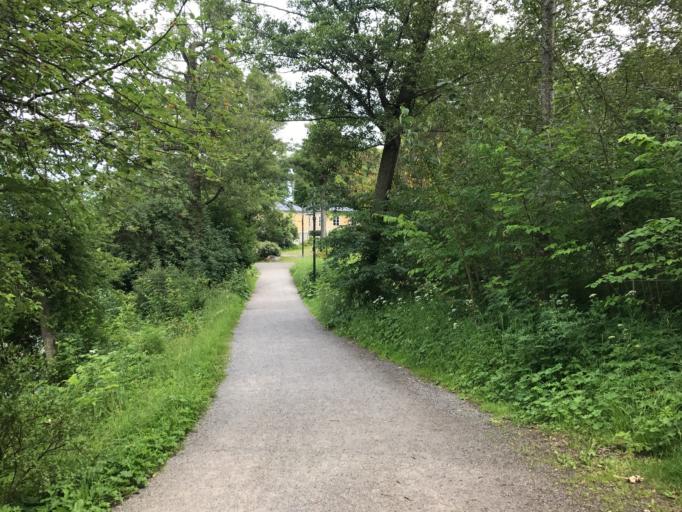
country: SE
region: Stockholm
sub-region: Stockholms Kommun
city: OEstermalm
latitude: 59.3300
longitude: 18.1153
